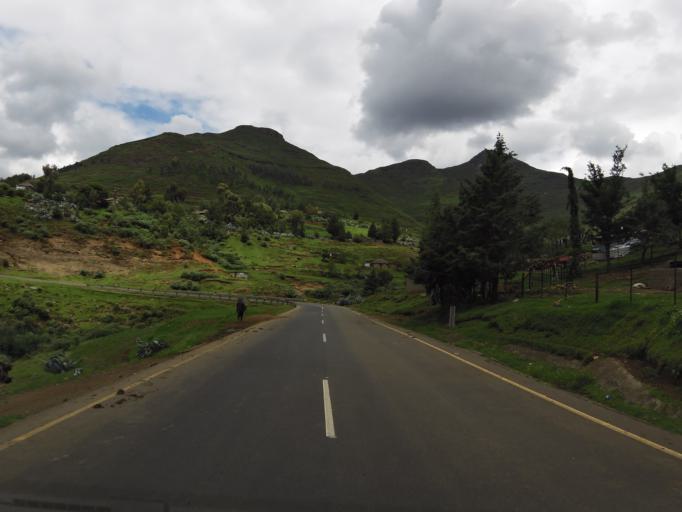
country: LS
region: Butha-Buthe
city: Butha-Buthe
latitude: -29.0366
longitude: 28.2916
